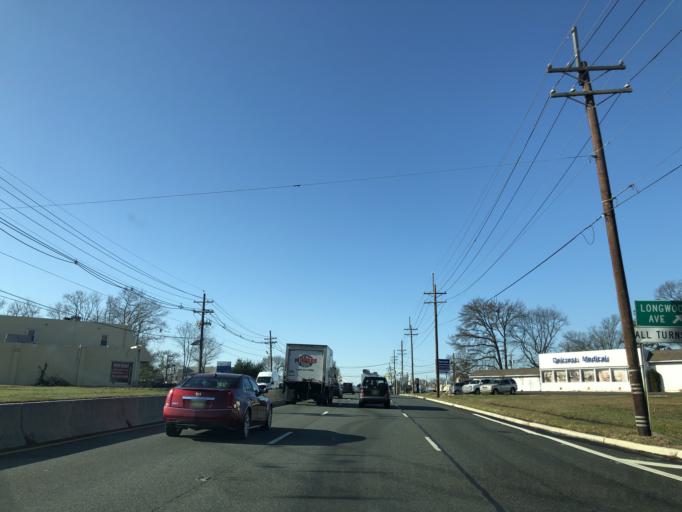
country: US
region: New Jersey
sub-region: Camden County
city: Golden Triangle
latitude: 39.9366
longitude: -75.0423
